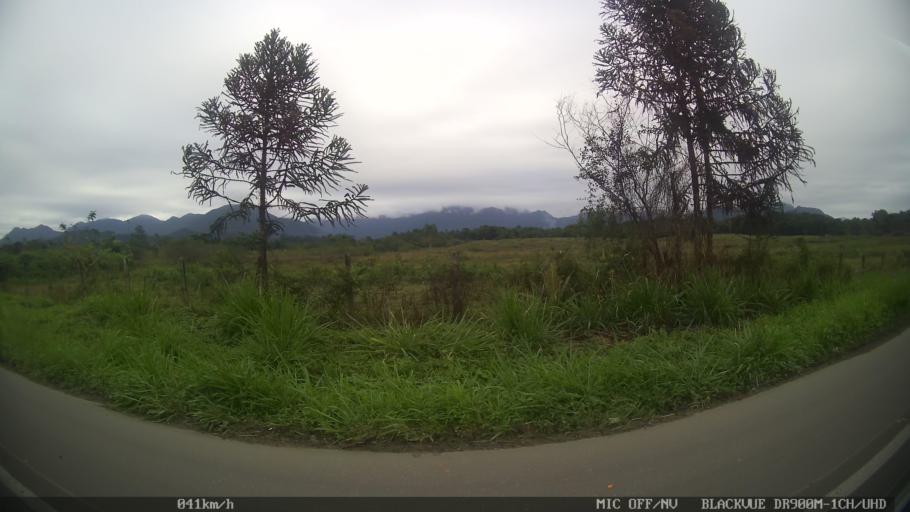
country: BR
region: Santa Catarina
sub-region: Joinville
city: Joinville
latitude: -26.3085
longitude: -48.9204
